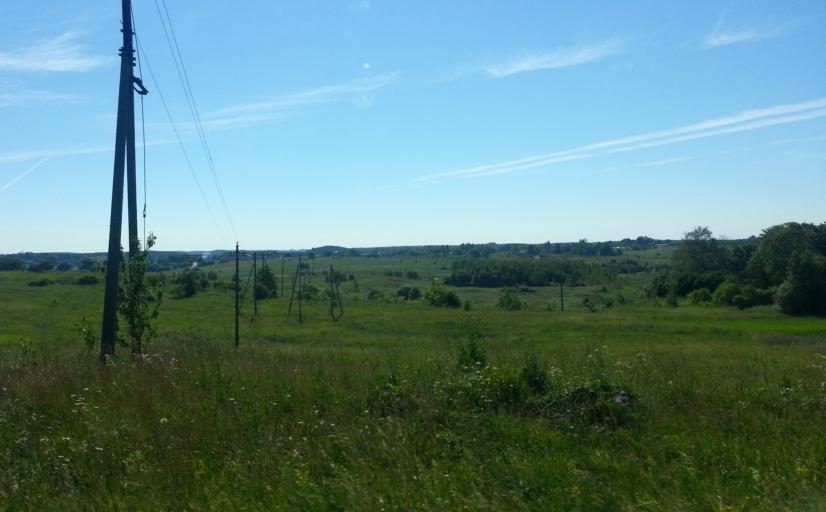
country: LT
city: Grigiskes
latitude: 54.7740
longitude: 25.0804
